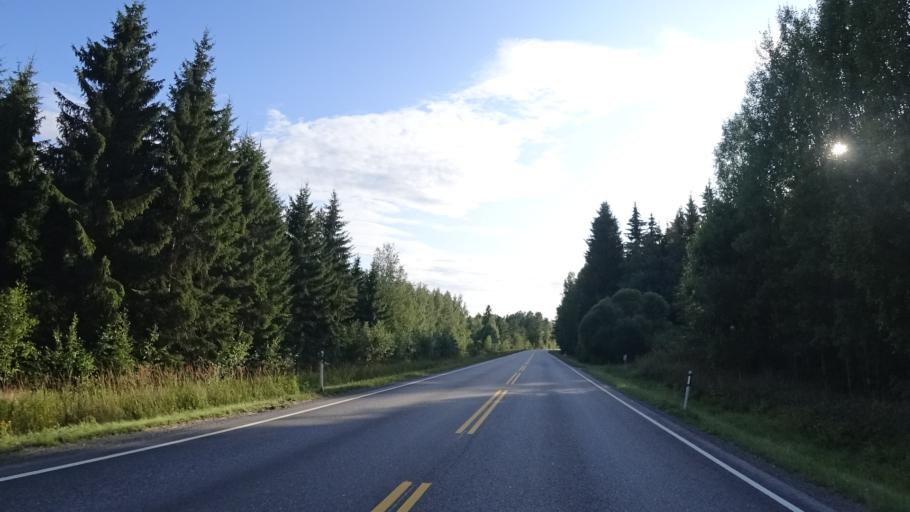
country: FI
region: South Karelia
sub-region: Imatra
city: Parikkala
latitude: 61.6113
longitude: 29.5135
